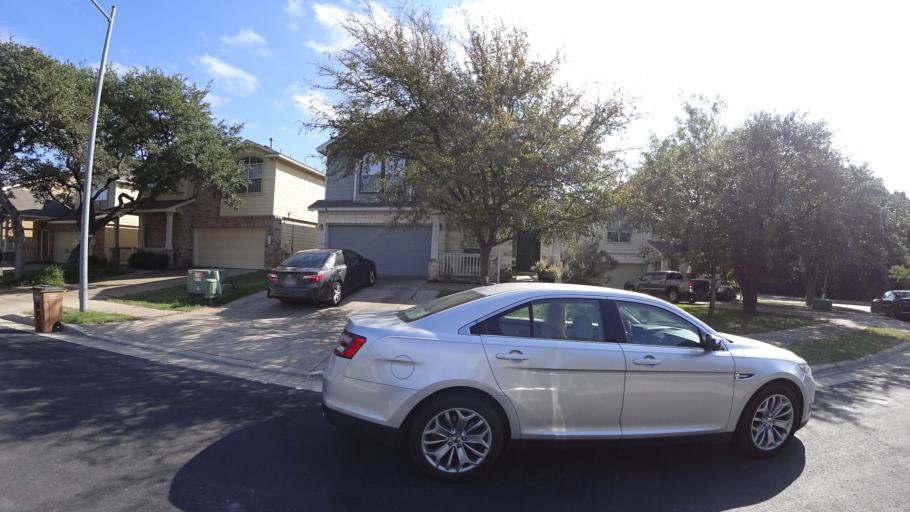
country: US
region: Texas
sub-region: Travis County
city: Shady Hollow
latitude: 30.1886
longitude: -97.8204
